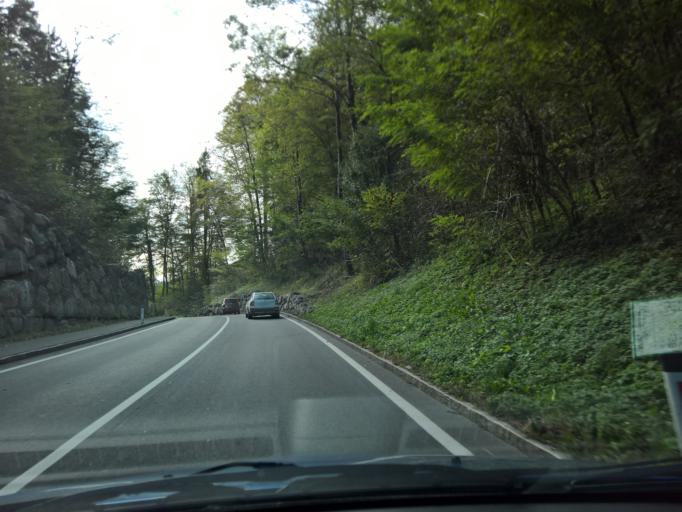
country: AT
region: Styria
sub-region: Politischer Bezirk Leibnitz
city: Grossklein
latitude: 46.7435
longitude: 15.4677
